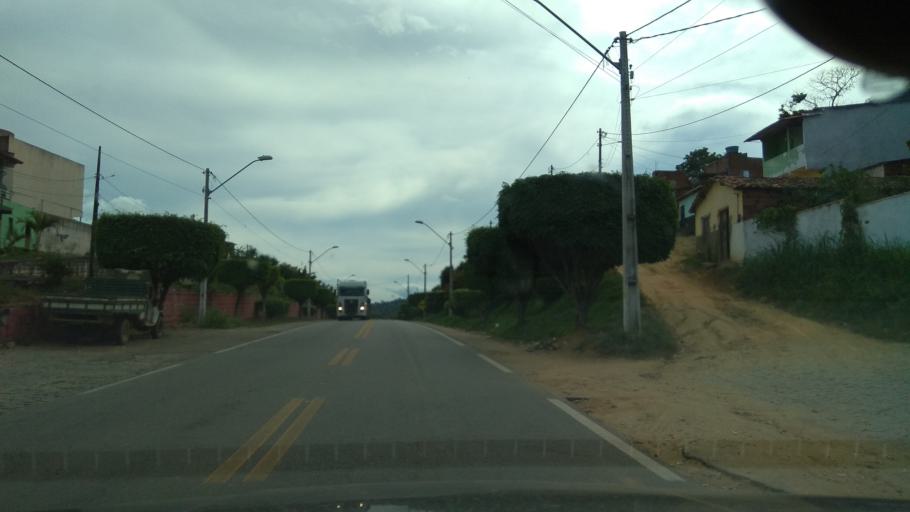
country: BR
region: Bahia
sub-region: Ubata
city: Ubata
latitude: -14.2116
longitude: -39.5198
